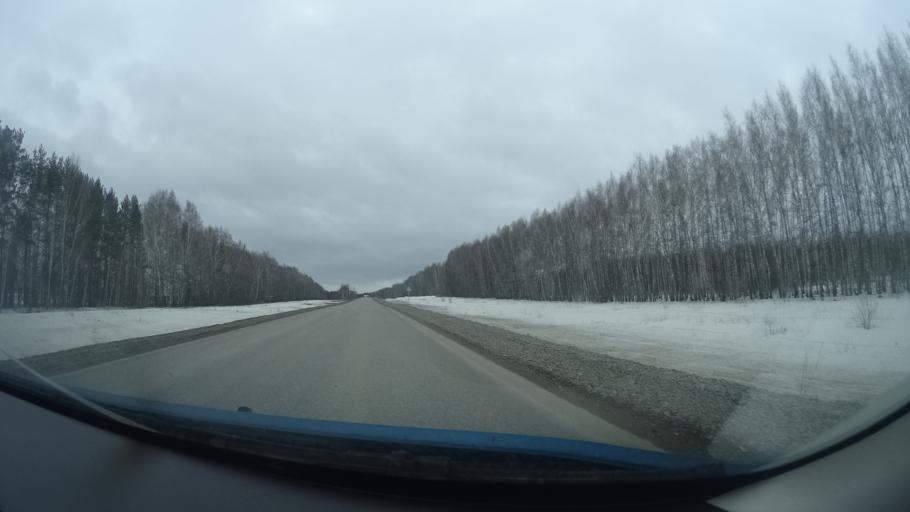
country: RU
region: Bashkortostan
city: Birsk
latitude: 55.3441
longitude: 55.5907
